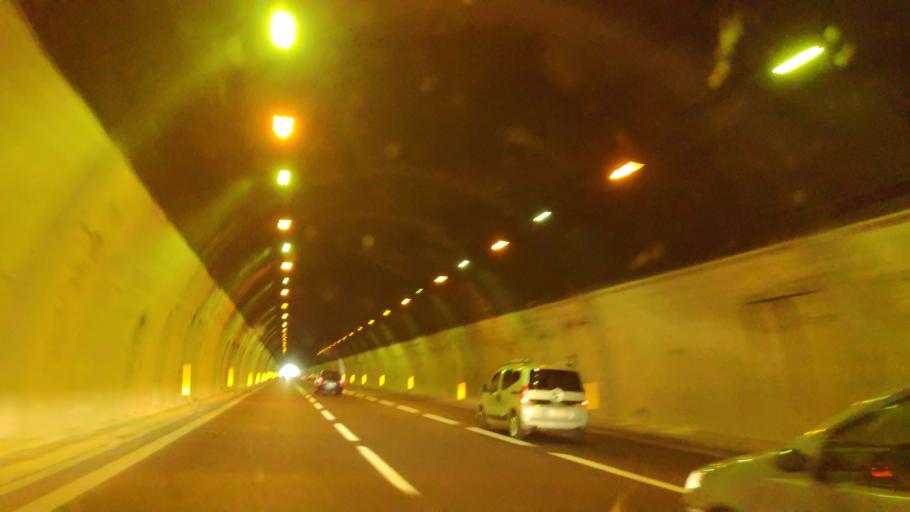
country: IT
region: Campania
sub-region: Provincia di Salerno
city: Lanzara
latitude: 40.7734
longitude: 14.6564
